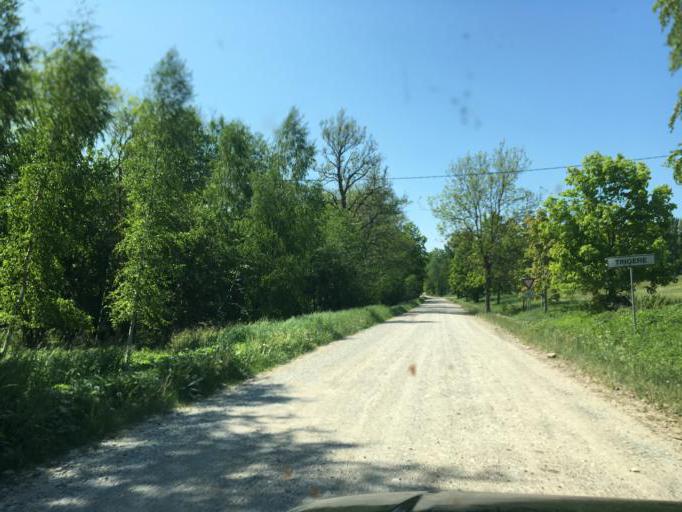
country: LV
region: Talsu Rajons
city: Valdemarpils
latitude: 57.4480
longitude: 22.5349
